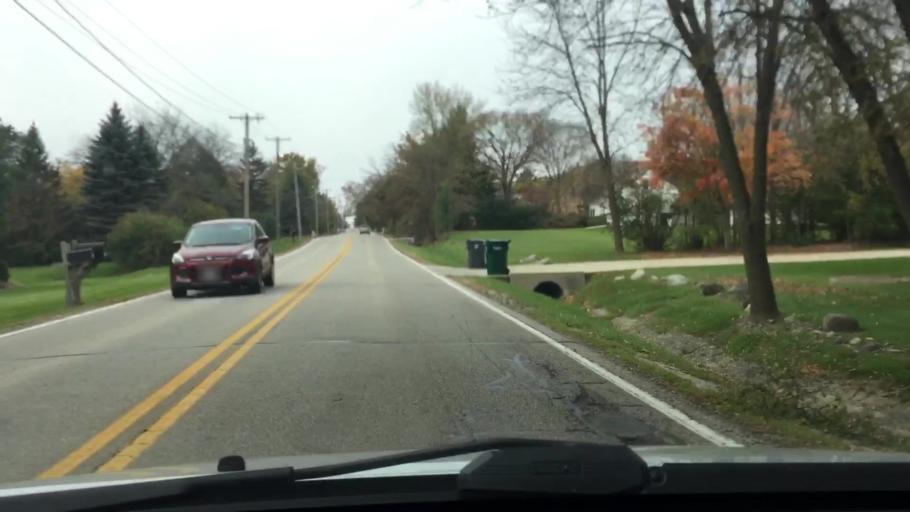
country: US
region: Wisconsin
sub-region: Milwaukee County
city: Hales Corners
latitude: 42.9445
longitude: -88.0731
